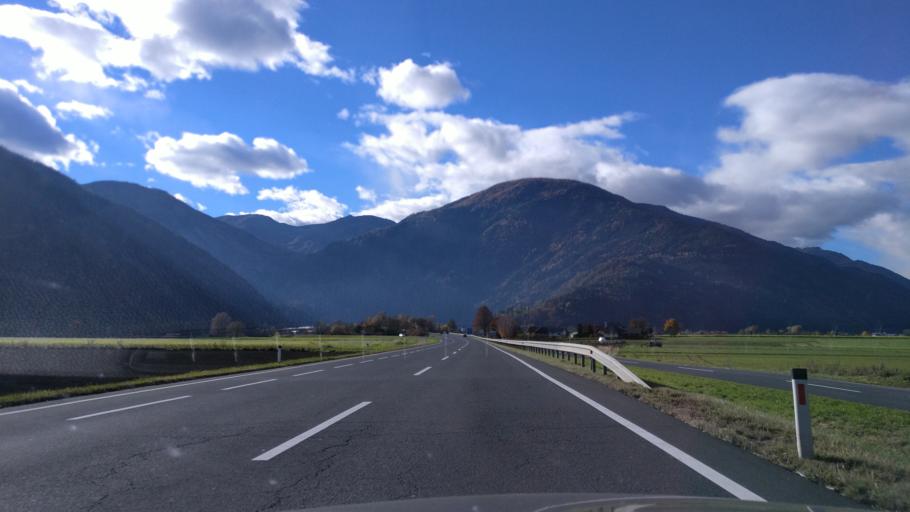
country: AT
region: Carinthia
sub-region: Politischer Bezirk Spittal an der Drau
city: Sachsenburg
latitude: 46.8327
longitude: 13.3921
